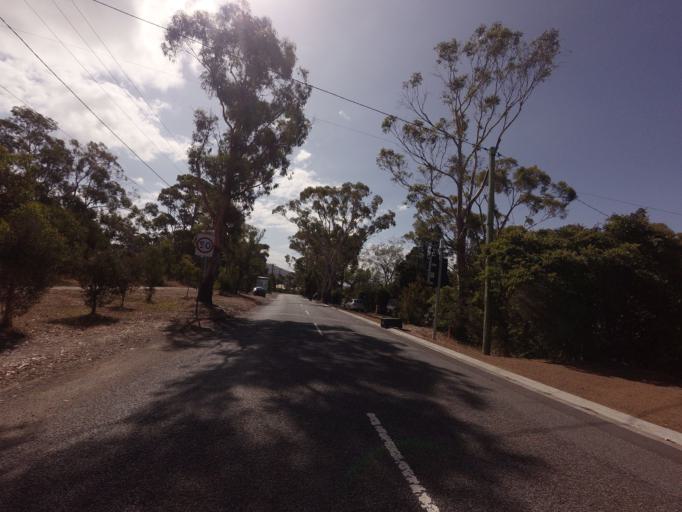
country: AU
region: Tasmania
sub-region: Hobart
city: Dynnyrne
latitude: -42.9125
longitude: 147.3231
